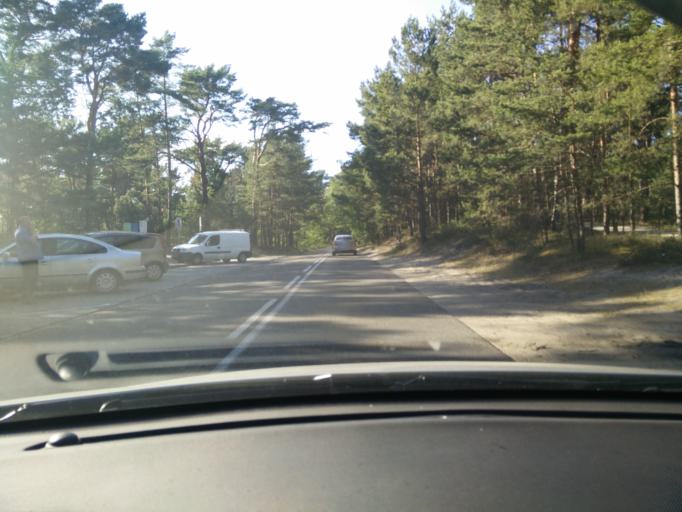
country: PL
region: Pomeranian Voivodeship
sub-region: Powiat pucki
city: Hel
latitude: 54.6223
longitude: 18.7974
